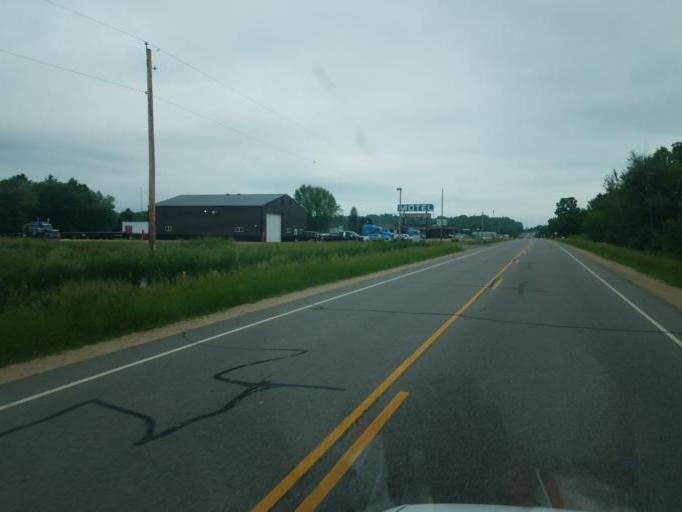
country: US
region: Wisconsin
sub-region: Juneau County
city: Elroy
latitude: 43.7255
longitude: -90.2660
